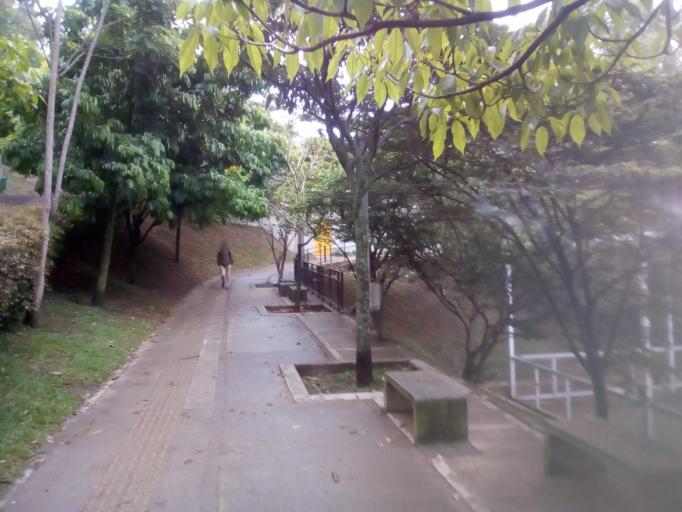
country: CO
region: Antioquia
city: Bello
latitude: 6.2969
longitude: -75.5718
